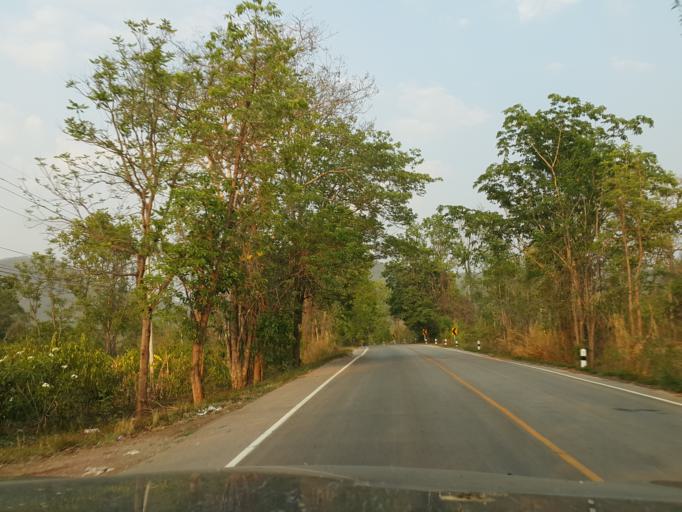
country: TH
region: Lamphun
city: Li
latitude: 17.8254
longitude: 98.9776
